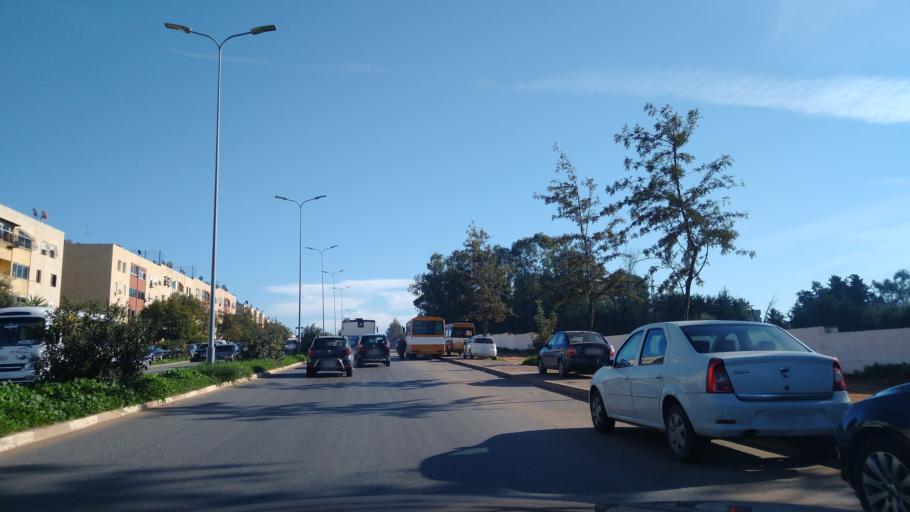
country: MA
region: Rabat-Sale-Zemmour-Zaer
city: Sale
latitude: 33.9986
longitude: -6.7493
